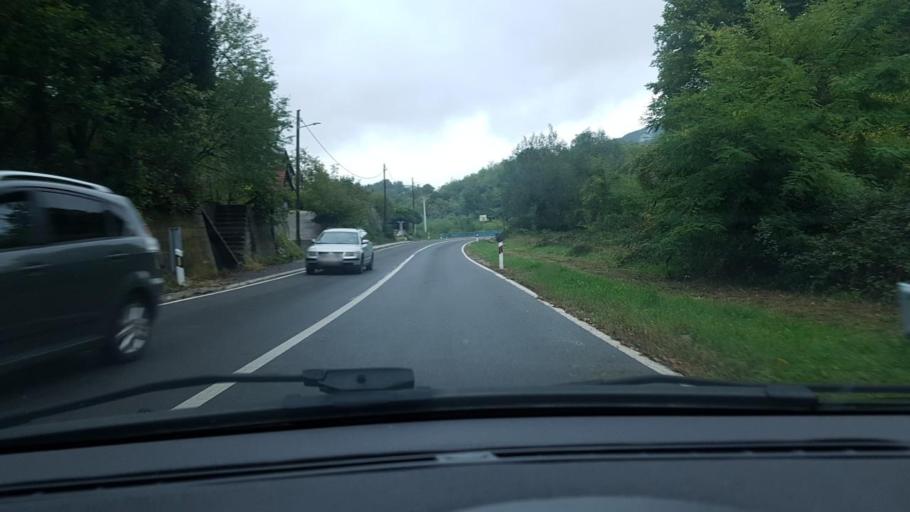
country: HR
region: Krapinsko-Zagorska
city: Marija Bistrica
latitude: 45.9751
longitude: 16.1014
